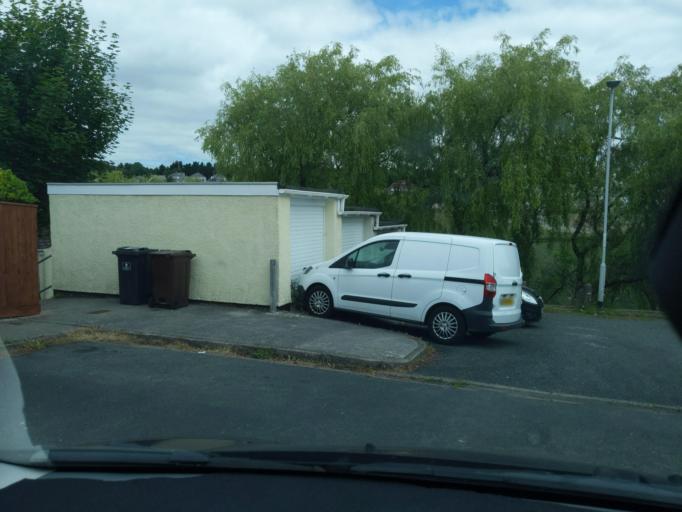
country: GB
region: England
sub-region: Plymouth
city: Plymouth
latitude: 50.4072
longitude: -4.1250
